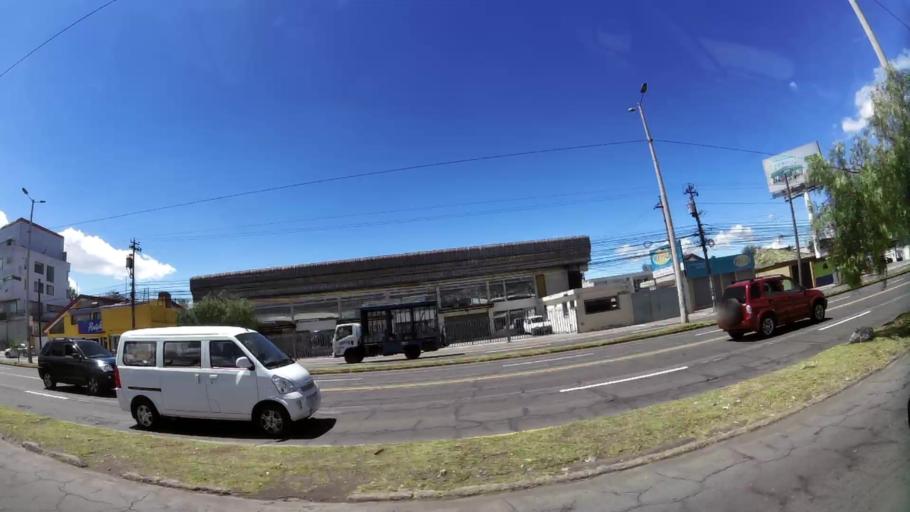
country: EC
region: Pichincha
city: Quito
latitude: -0.1542
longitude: -78.4848
